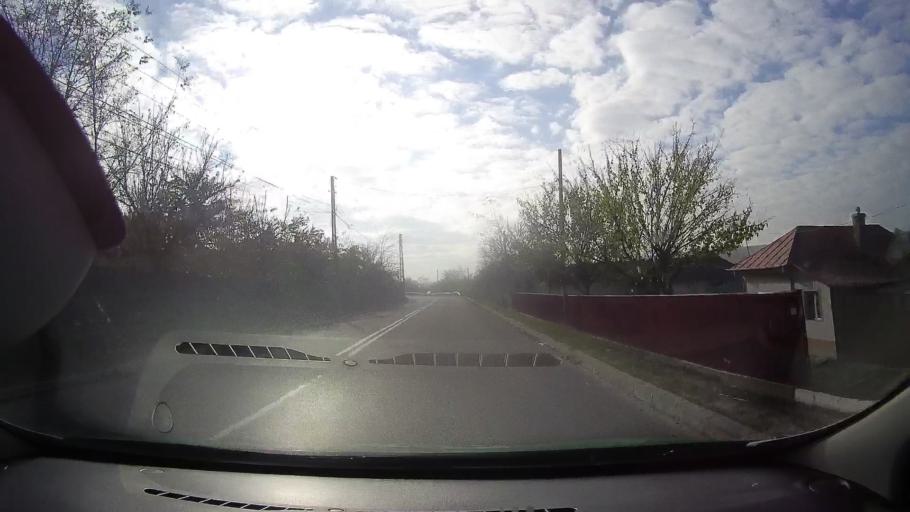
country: RO
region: Tulcea
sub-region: Comuna Bestepe
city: Bestepe
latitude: 45.0869
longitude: 29.0188
